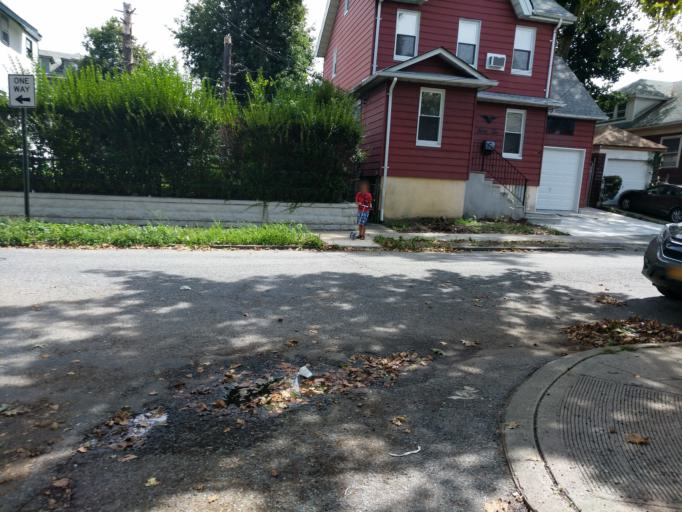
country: US
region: New Jersey
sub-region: Hudson County
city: Bayonne
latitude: 40.6213
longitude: -74.0734
